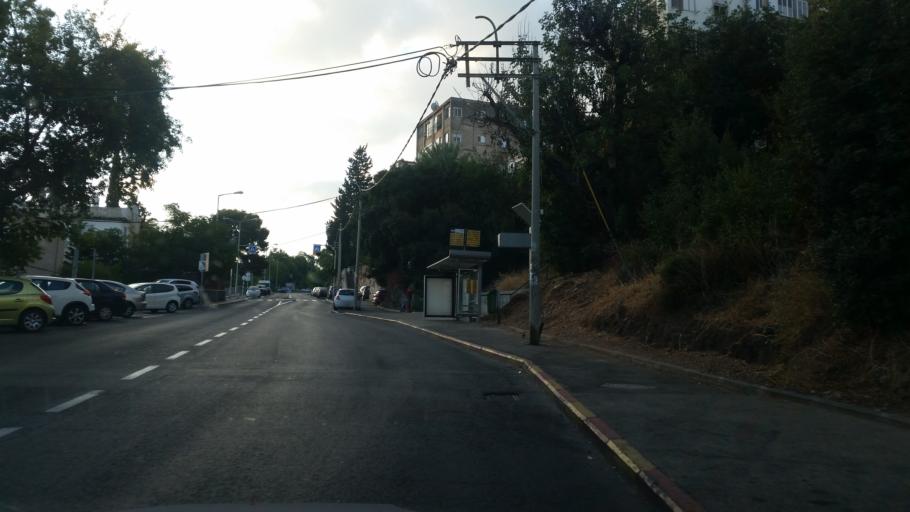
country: IL
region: Haifa
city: Haifa
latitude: 32.7995
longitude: 35.0125
